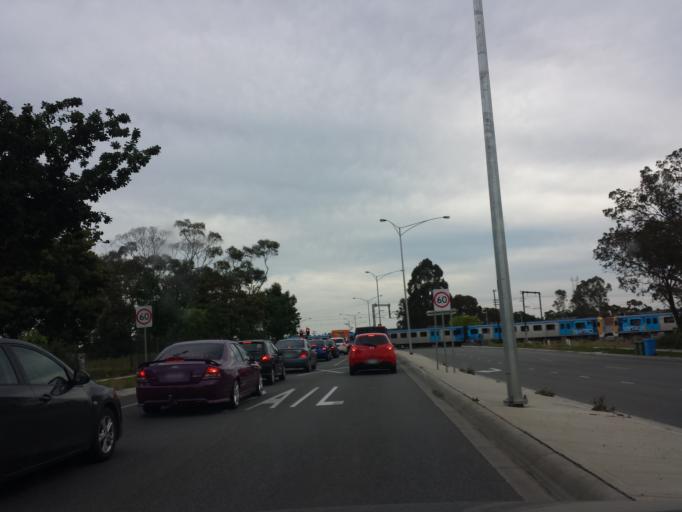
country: AU
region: Victoria
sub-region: Casey
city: Berwick
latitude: -38.0362
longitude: 145.3428
